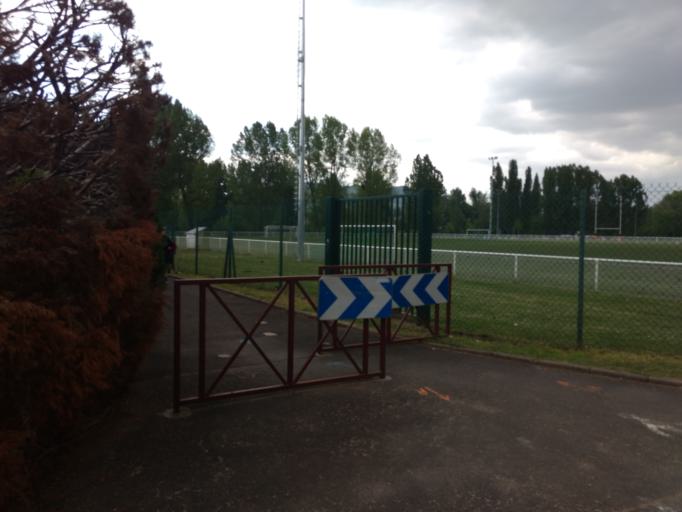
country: FR
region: Auvergne
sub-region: Departement du Puy-de-Dome
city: Pont-du-Chateau
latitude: 45.7954
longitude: 3.2470
